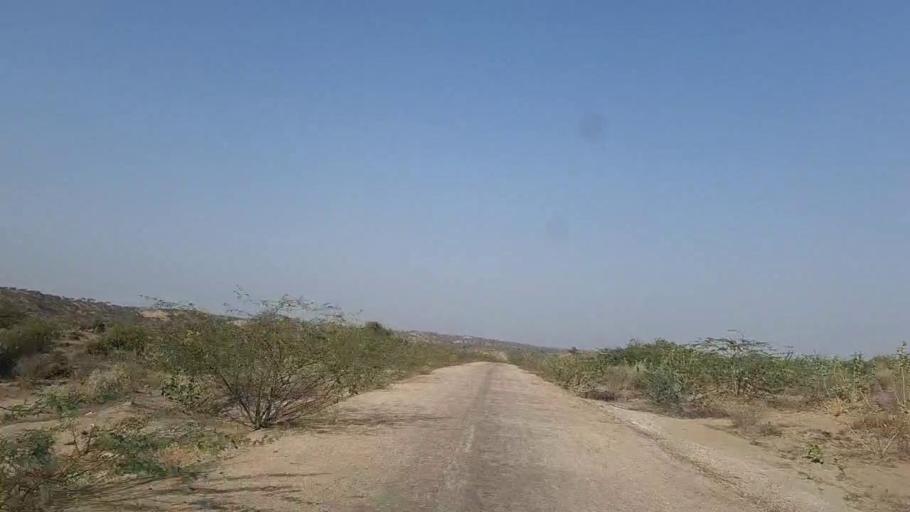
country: PK
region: Sindh
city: Naukot
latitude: 24.6219
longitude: 69.3500
